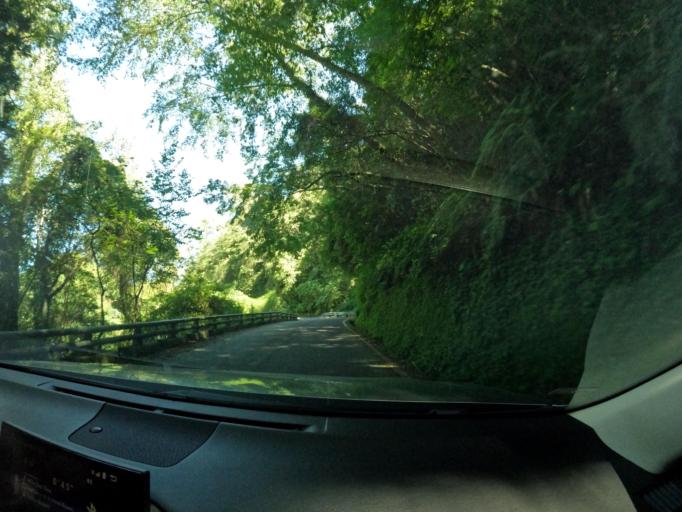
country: TW
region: Taiwan
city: Yujing
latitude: 23.2800
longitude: 120.8947
